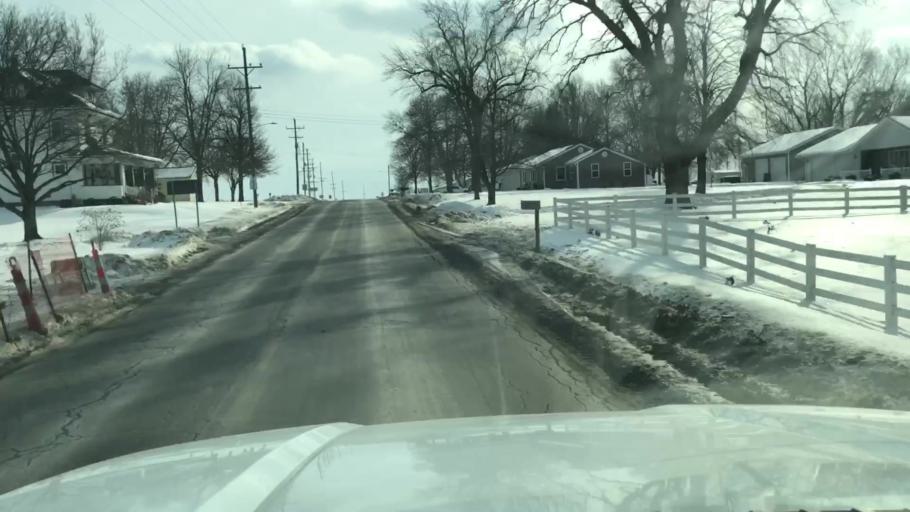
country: US
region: Missouri
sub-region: Gentry County
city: Stanberry
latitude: 40.3498
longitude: -94.6733
